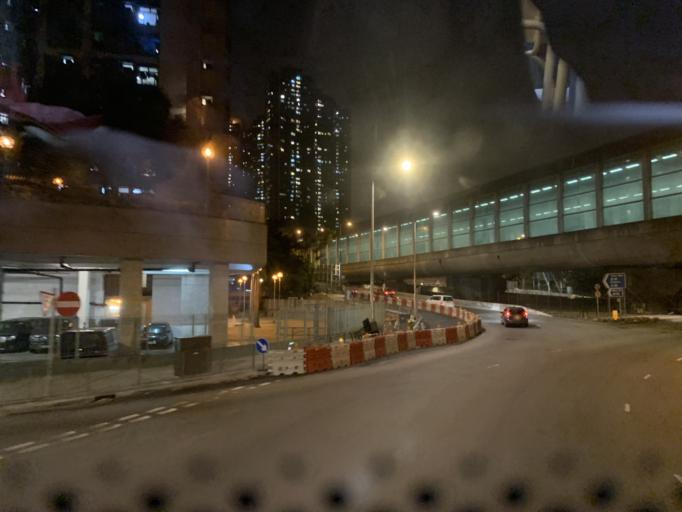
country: HK
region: Tsuen Wan
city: Tsuen Wan
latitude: 22.3601
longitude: 114.1031
